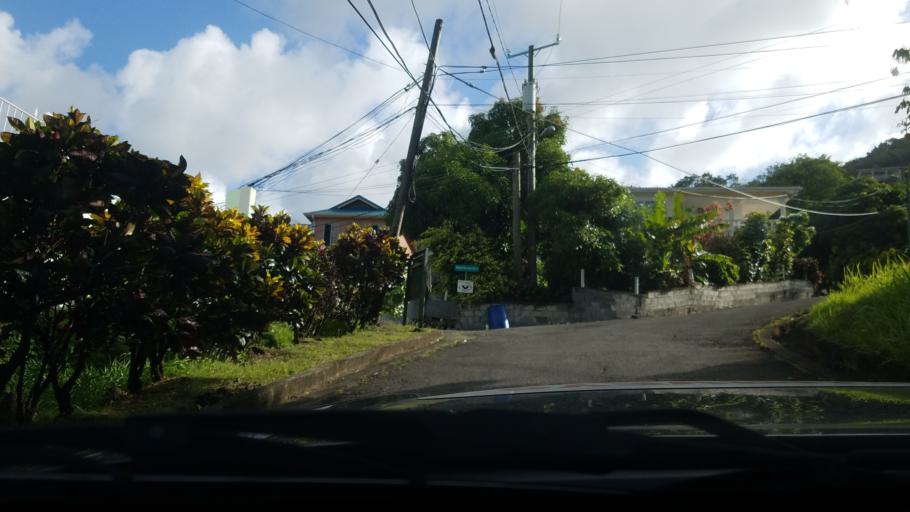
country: LC
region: Castries Quarter
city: Bisee
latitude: 14.0374
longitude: -60.9541
